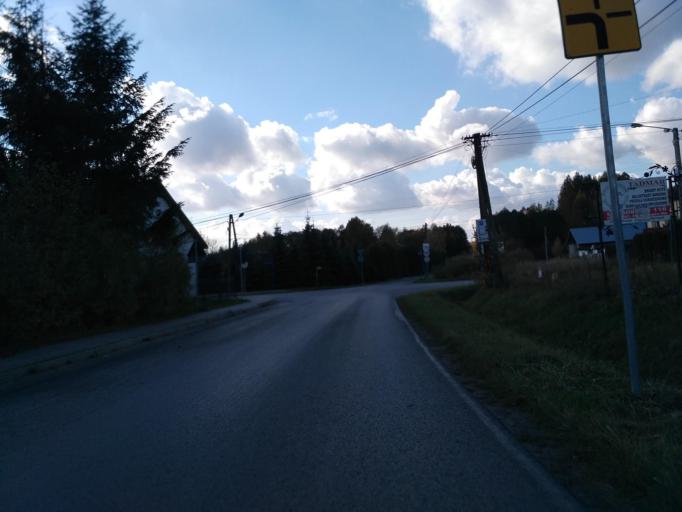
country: PL
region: Subcarpathian Voivodeship
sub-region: Powiat rzeszowski
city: Glogow Malopolski
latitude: 50.1443
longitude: 21.9484
